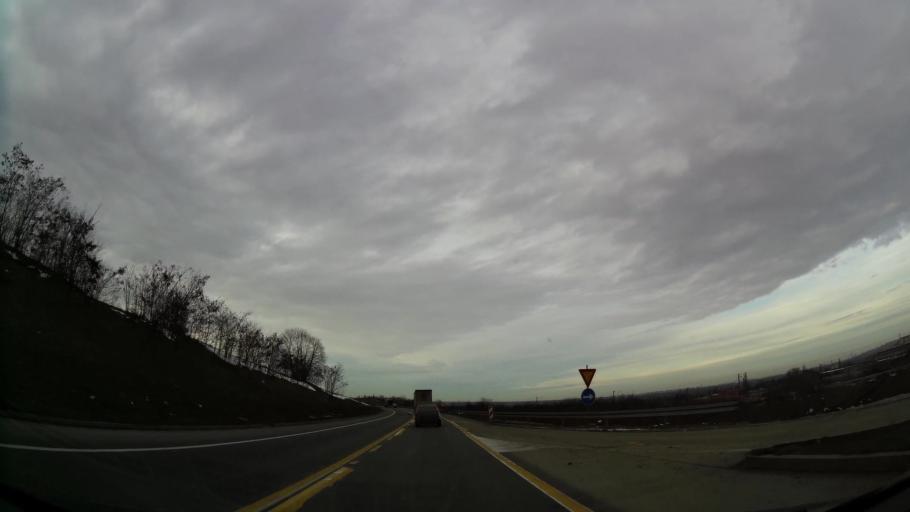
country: RS
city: Ostruznica
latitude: 44.7220
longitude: 20.3587
